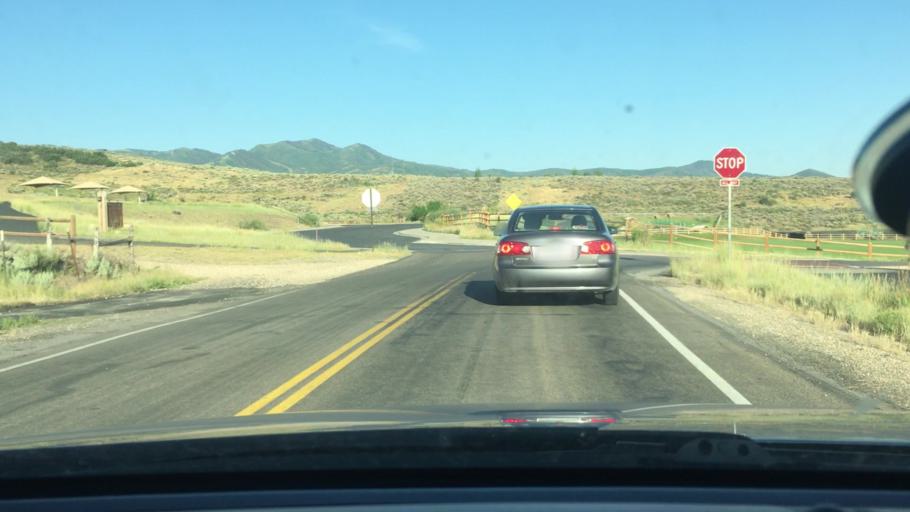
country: US
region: Utah
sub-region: Summit County
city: Snyderville
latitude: 40.7123
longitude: -111.5014
